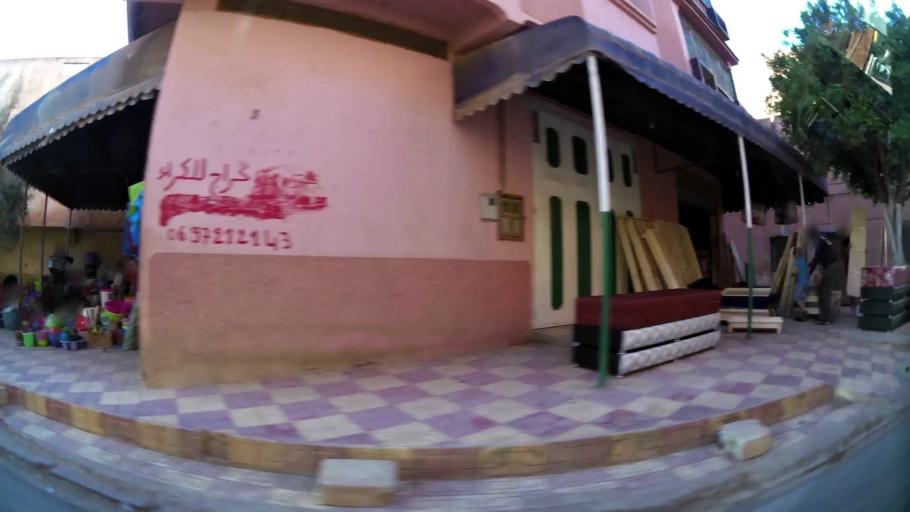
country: MA
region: Oriental
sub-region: Berkane-Taourirt
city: Berkane
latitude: 34.9218
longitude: -2.3161
